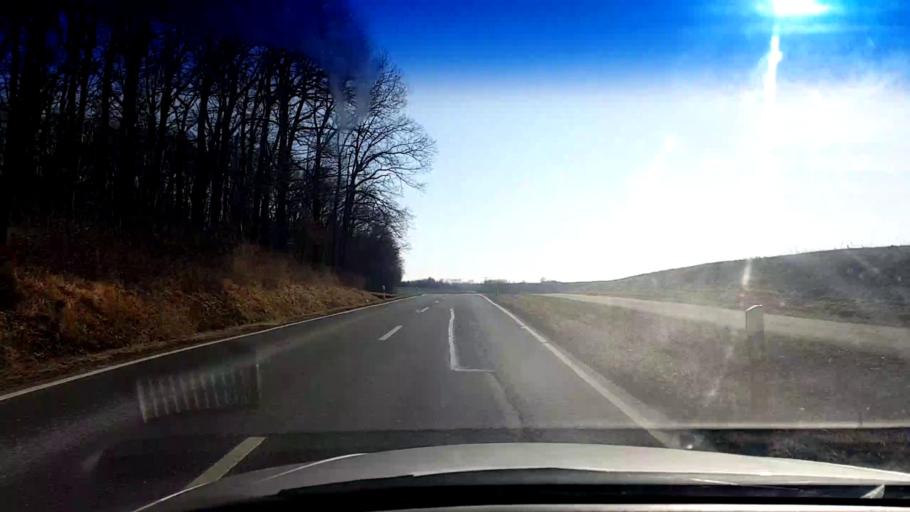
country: DE
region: Bavaria
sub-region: Upper Franconia
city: Litzendorf
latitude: 49.8780
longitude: 11.0198
